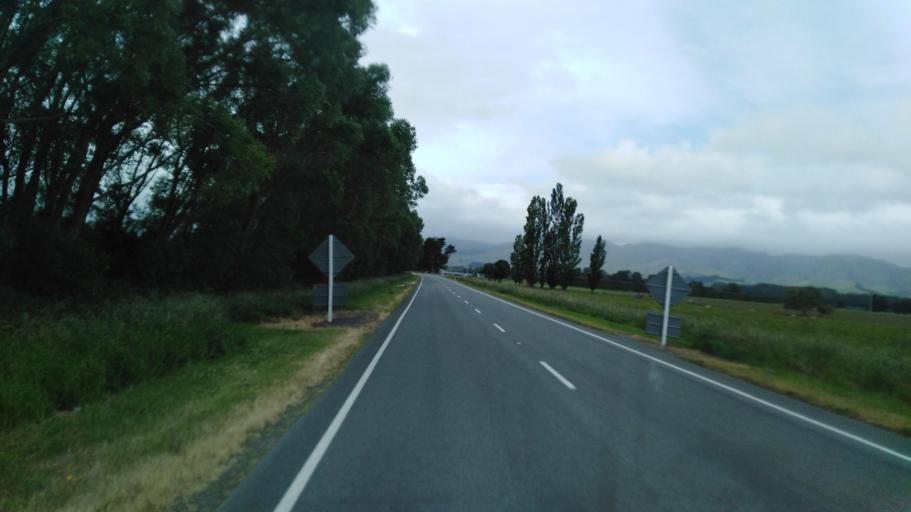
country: NZ
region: Canterbury
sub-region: Kaikoura District
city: Kaikoura
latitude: -42.7375
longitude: 173.2685
